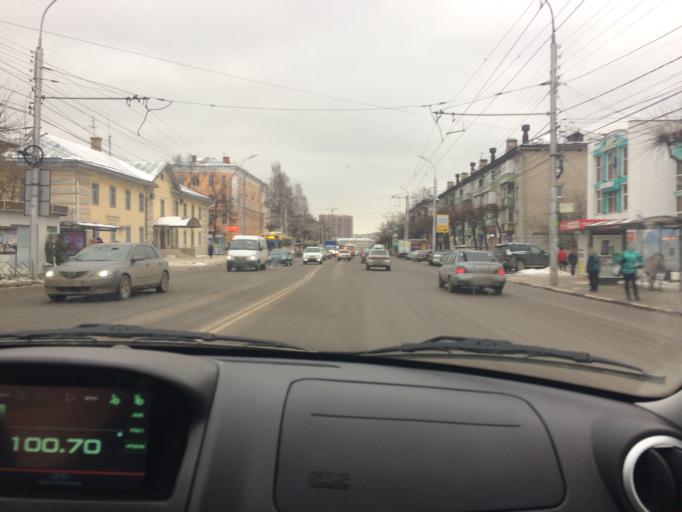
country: RU
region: Rjazan
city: Ryazan'
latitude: 54.6204
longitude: 39.7242
